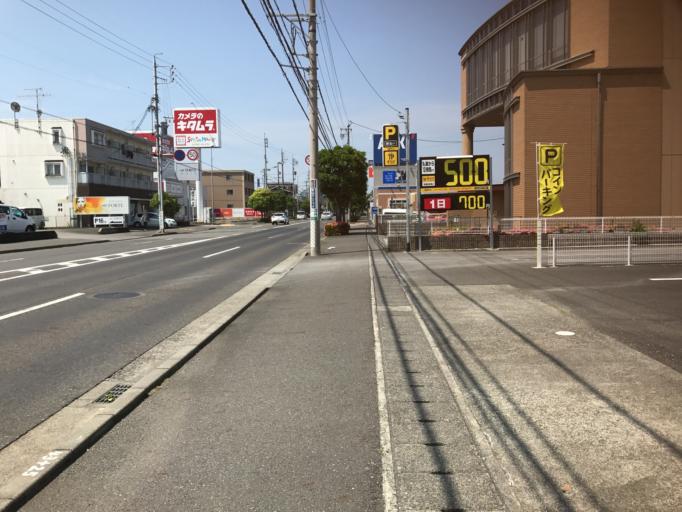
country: JP
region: Shizuoka
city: Shizuoka-shi
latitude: 35.0000
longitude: 138.4420
